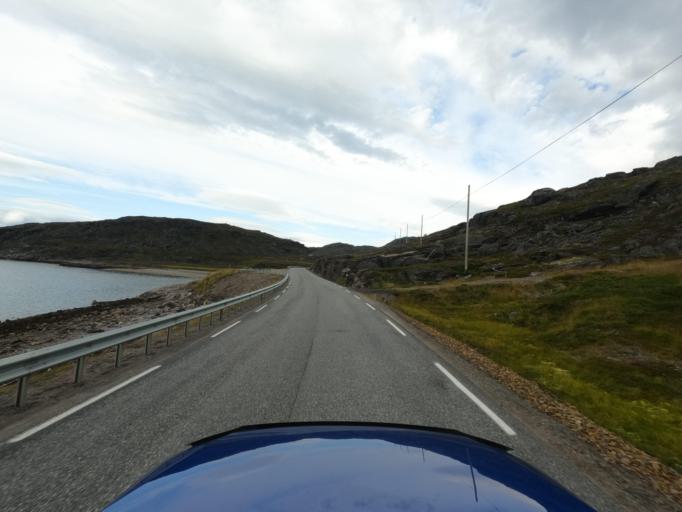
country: NO
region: Finnmark Fylke
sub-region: Hammerfest
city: Rypefjord
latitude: 70.5934
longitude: 23.6818
